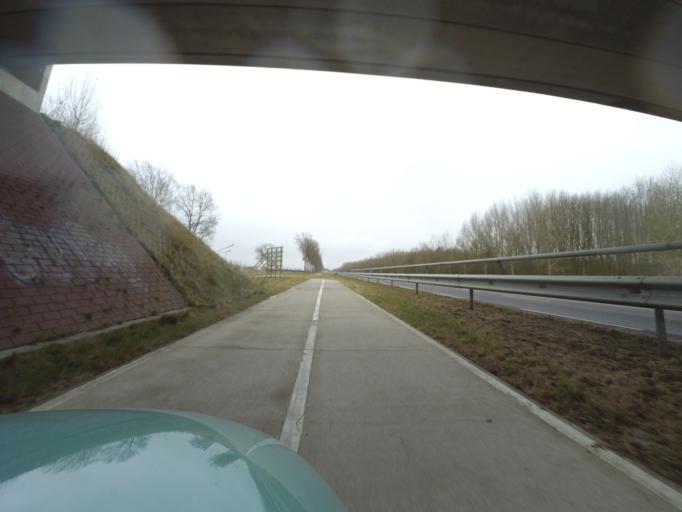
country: NL
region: Flevoland
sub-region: Gemeente Dronten
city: Dronten
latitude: 52.5323
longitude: 5.7384
